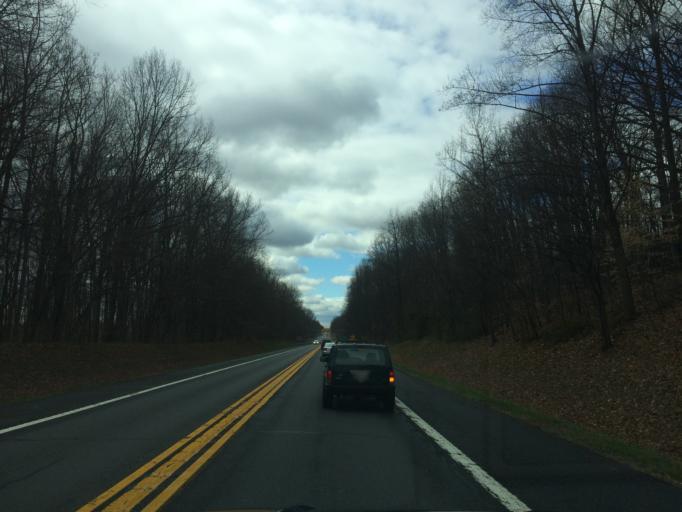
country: US
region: Maryland
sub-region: Frederick County
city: Jefferson
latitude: 39.3431
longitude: -77.5073
